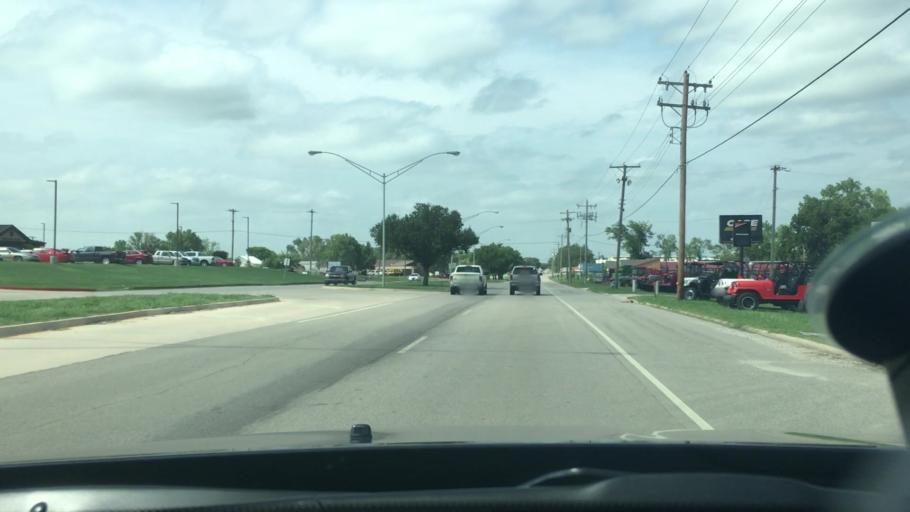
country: US
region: Oklahoma
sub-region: Pontotoc County
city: Ada
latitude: 34.7949
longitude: -96.6786
